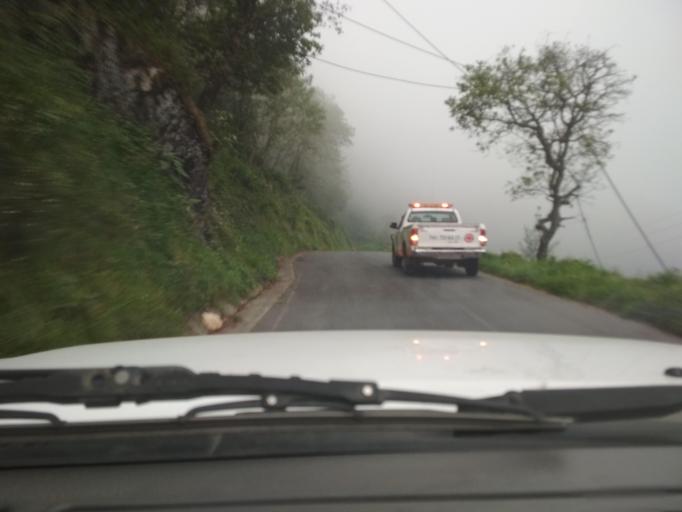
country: MX
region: Veracruz
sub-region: La Perla
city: Metlac Hernandez (Metlac Primero)
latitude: 18.9685
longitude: -97.1465
